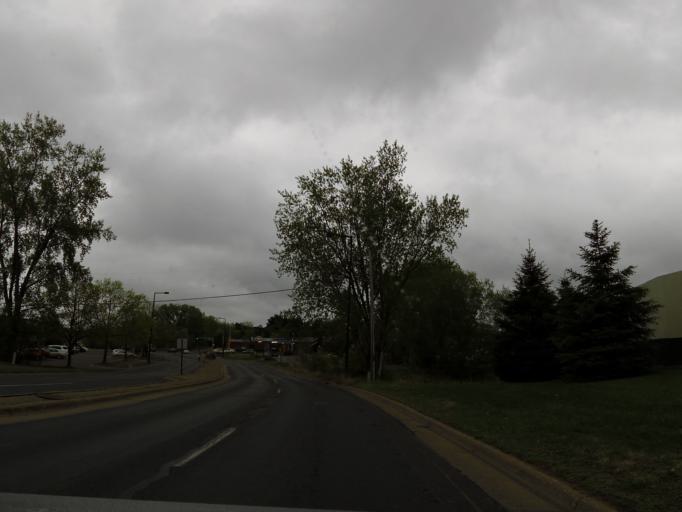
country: US
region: Minnesota
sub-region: Washington County
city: Stillwater
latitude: 45.0409
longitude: -92.8237
